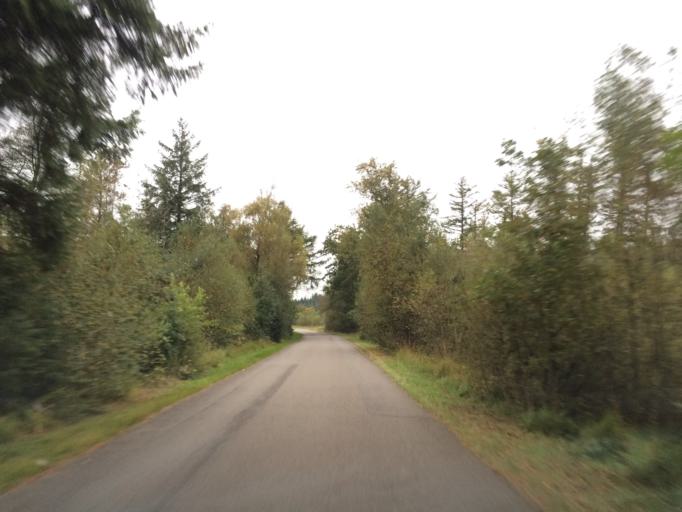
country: DK
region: Central Jutland
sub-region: Holstebro Kommune
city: Ulfborg
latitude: 56.2319
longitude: 8.4367
